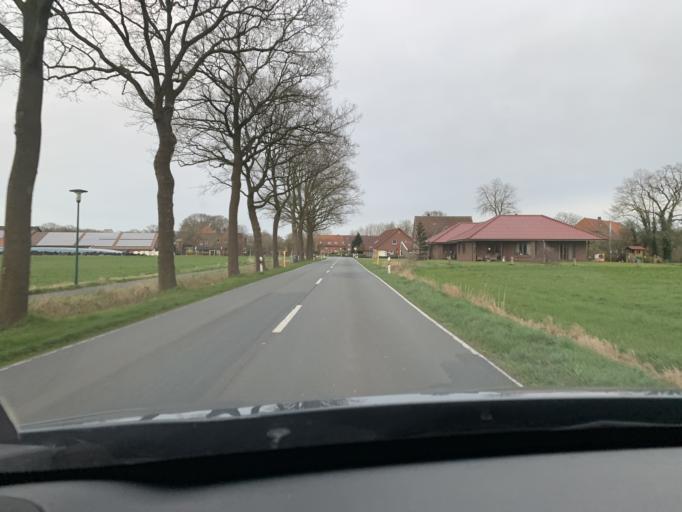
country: DE
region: Lower Saxony
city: Barssel
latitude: 53.1756
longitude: 7.7705
